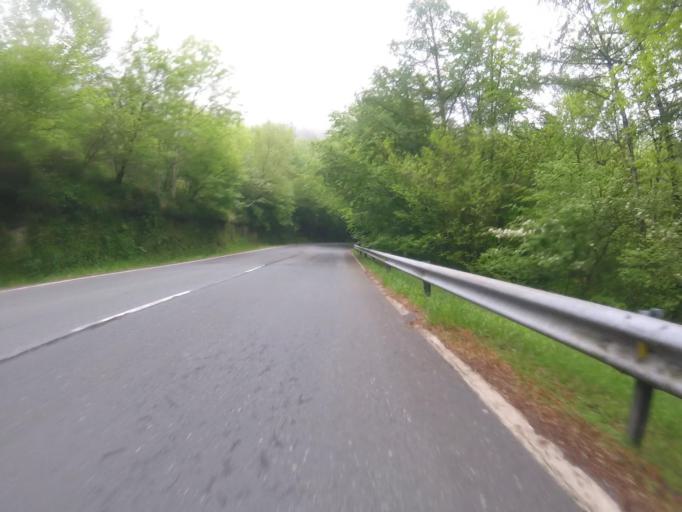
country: ES
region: Navarre
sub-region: Provincia de Navarra
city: Zugarramurdi
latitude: 43.2423
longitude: -1.4817
